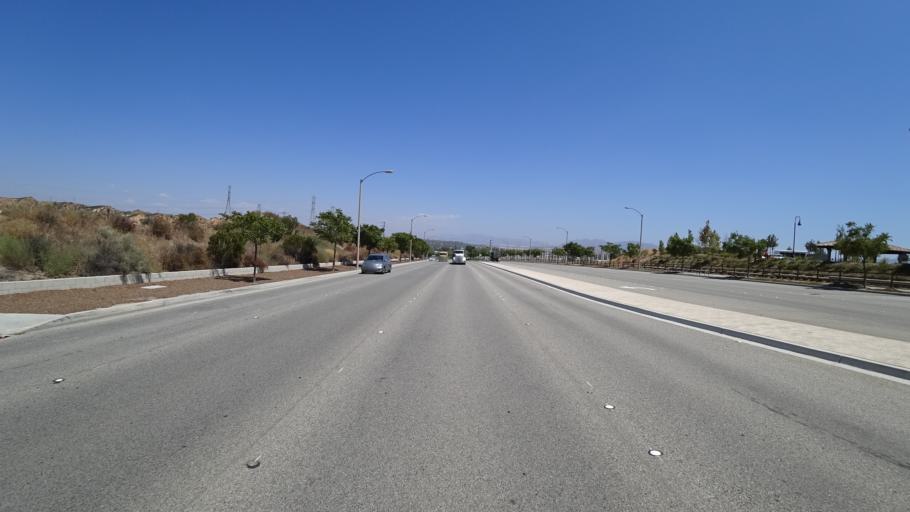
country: US
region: California
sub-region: Los Angeles County
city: Valencia
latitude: 34.4418
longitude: -118.5915
